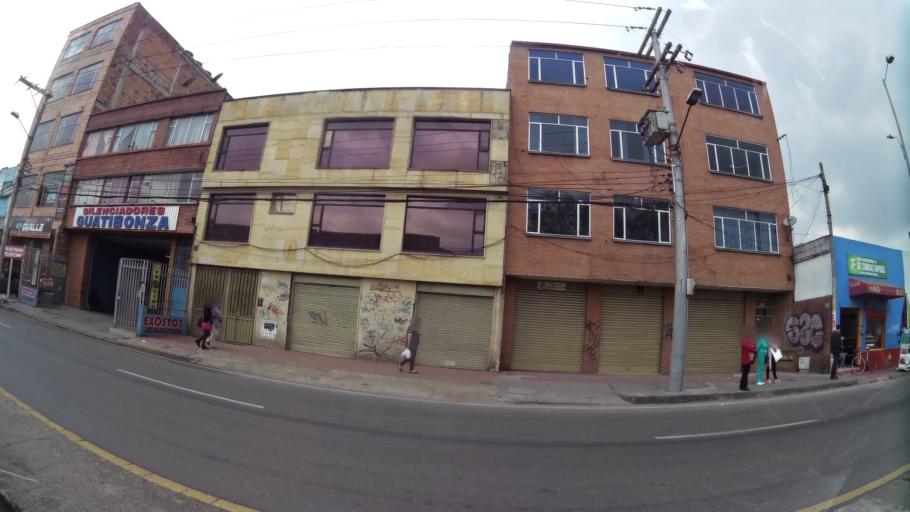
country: CO
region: Bogota D.C.
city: Bogota
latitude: 4.5860
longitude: -74.0948
